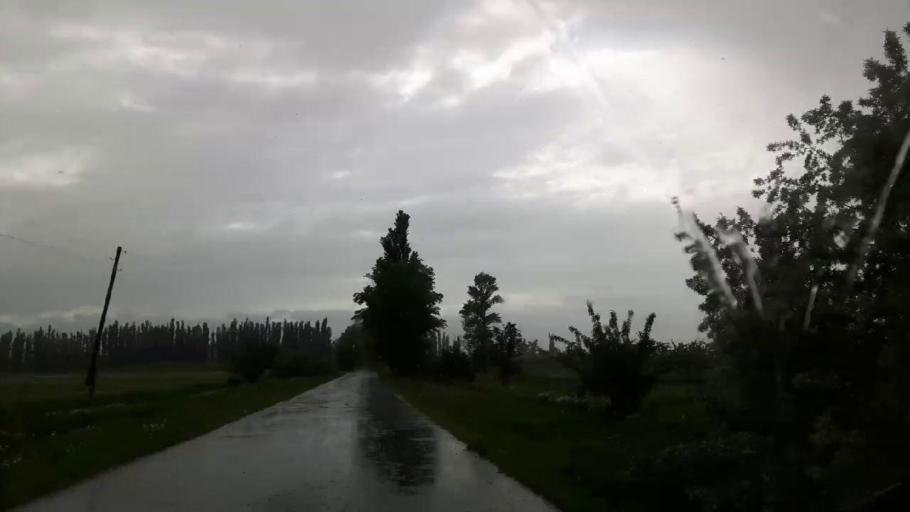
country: GE
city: Agara
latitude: 42.0113
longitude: 43.7807
